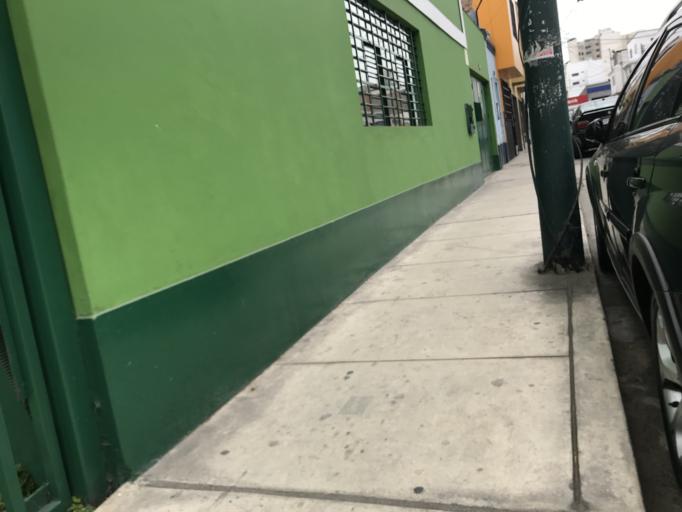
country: PE
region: Lima
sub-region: Lima
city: San Isidro
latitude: -12.0931
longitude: -77.0716
